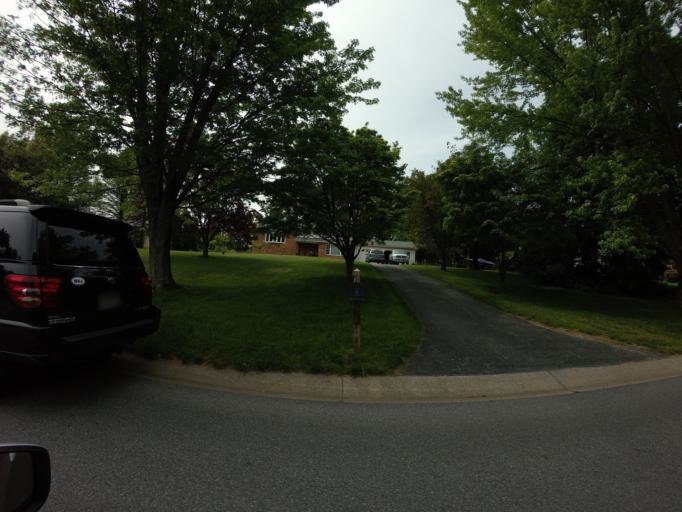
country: US
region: Maryland
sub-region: Carroll County
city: Eldersburg
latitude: 39.4655
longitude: -76.9606
